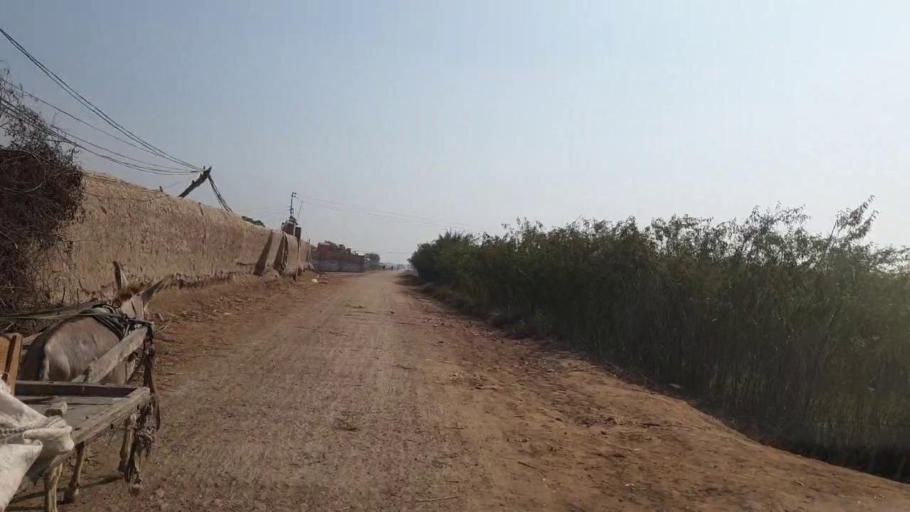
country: PK
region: Sindh
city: Bhit Shah
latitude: 25.7273
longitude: 68.5340
